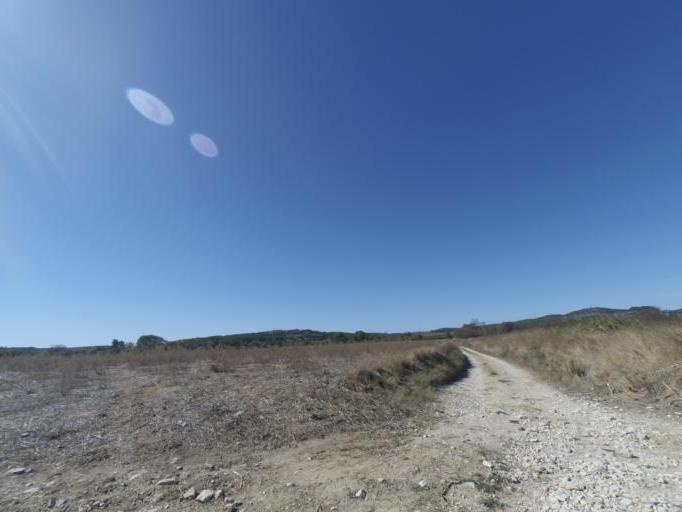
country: FR
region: Languedoc-Roussillon
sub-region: Departement du Gard
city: Vergeze
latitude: 43.7654
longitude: 4.2164
